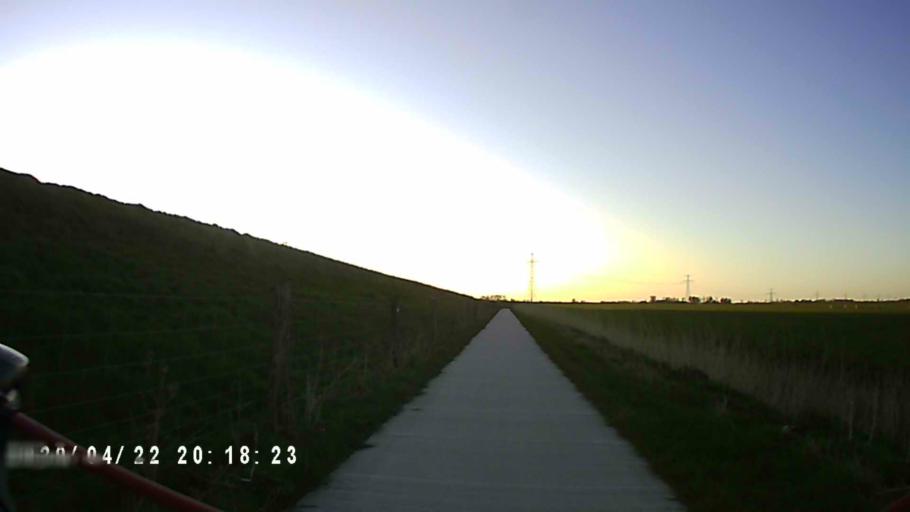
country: NL
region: Groningen
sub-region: Gemeente Winsum
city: Winsum
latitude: 53.3091
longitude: 6.4919
